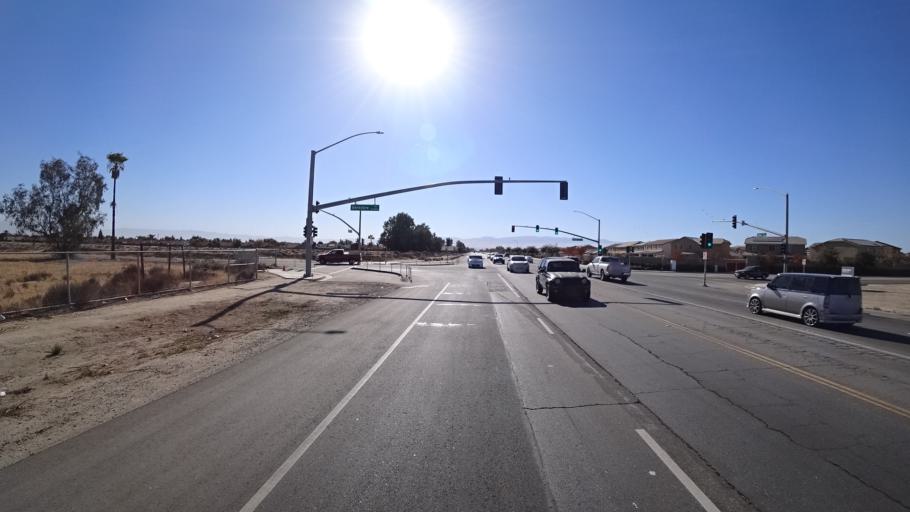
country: US
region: California
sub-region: Kern County
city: Greenfield
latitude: 35.2891
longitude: -119.0566
